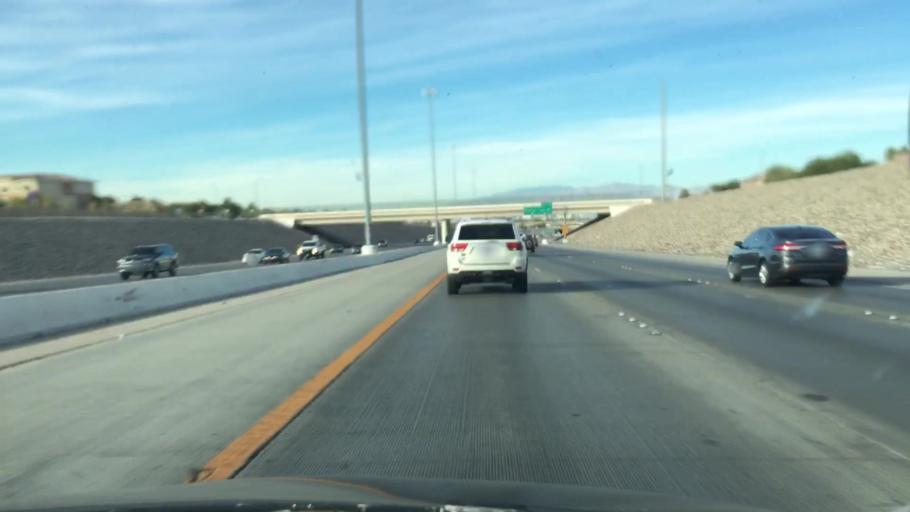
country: US
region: Nevada
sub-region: Clark County
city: Whitney
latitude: 36.0335
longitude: -115.1324
